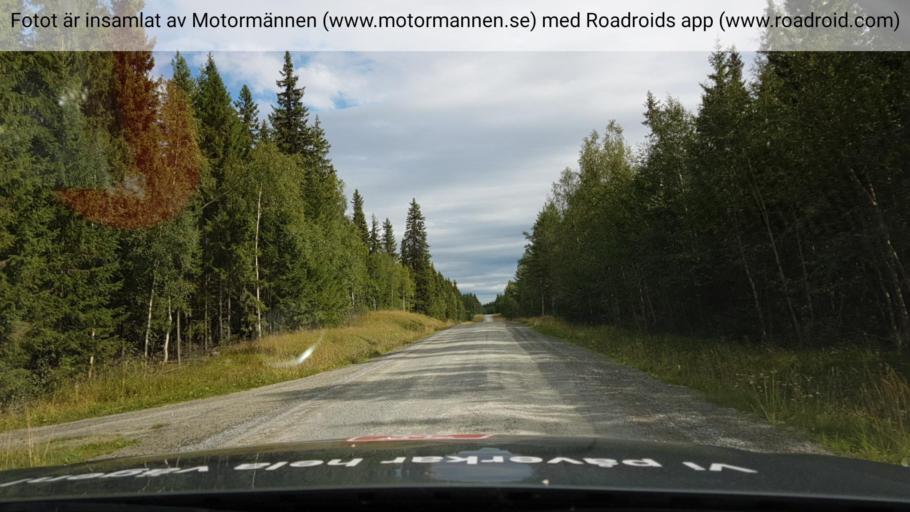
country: SE
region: Jaemtland
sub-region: Krokoms Kommun
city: Valla
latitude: 63.6486
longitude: 13.8105
